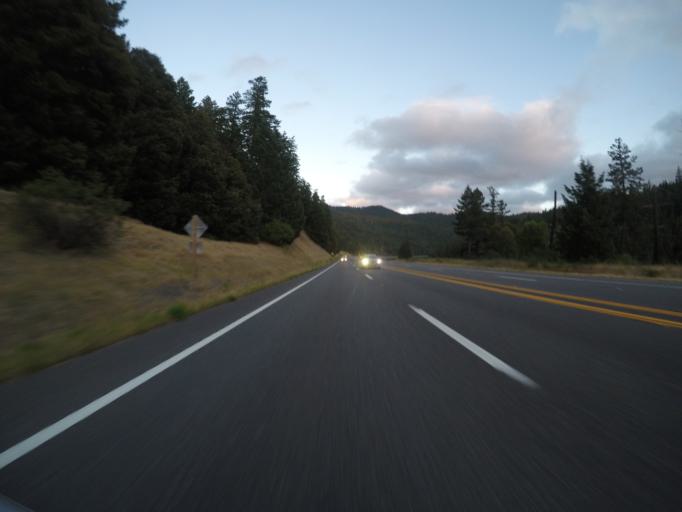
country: US
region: California
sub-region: Humboldt County
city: Redway
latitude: 40.0413
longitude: -123.7792
